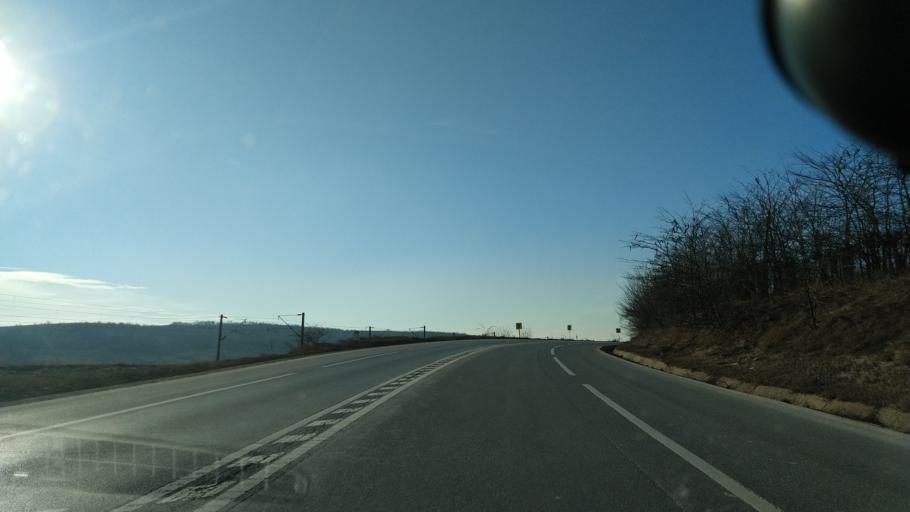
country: RO
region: Iasi
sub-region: Comuna Baltati
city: Baltati
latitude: 47.2227
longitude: 27.1765
